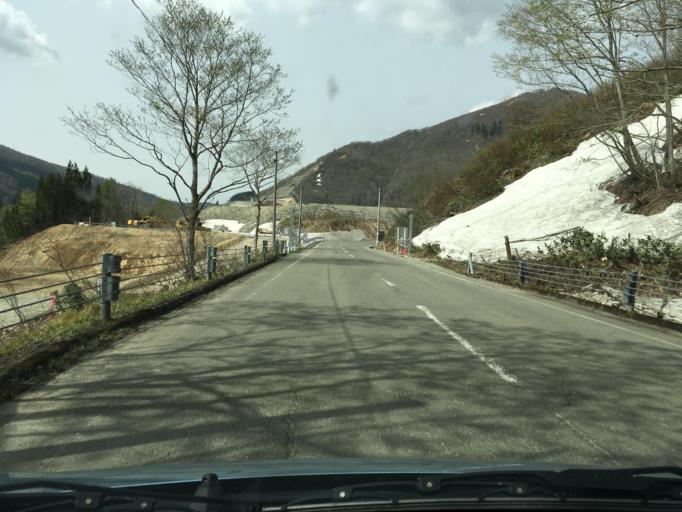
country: JP
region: Akita
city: Yuzawa
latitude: 39.0294
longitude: 140.7276
